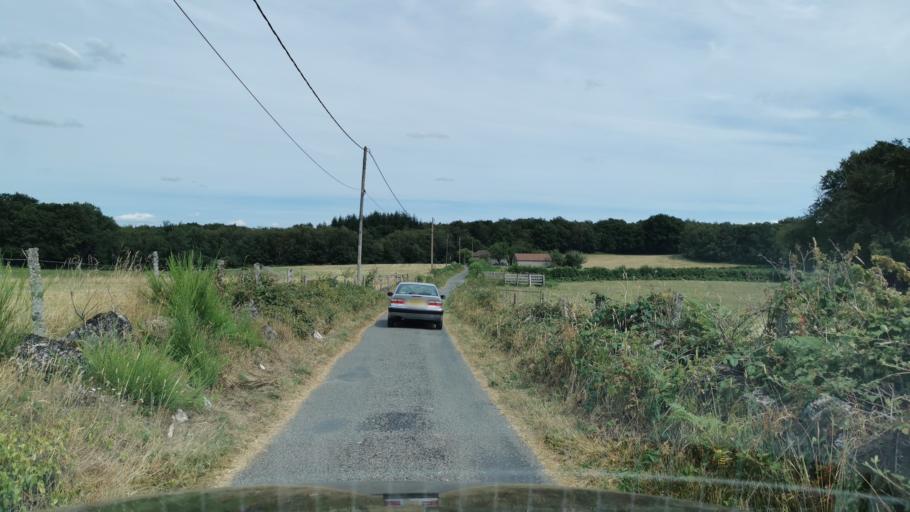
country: FR
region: Bourgogne
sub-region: Departement de Saone-et-Loire
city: Etang-sur-Arroux
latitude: 46.8017
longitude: 4.2637
